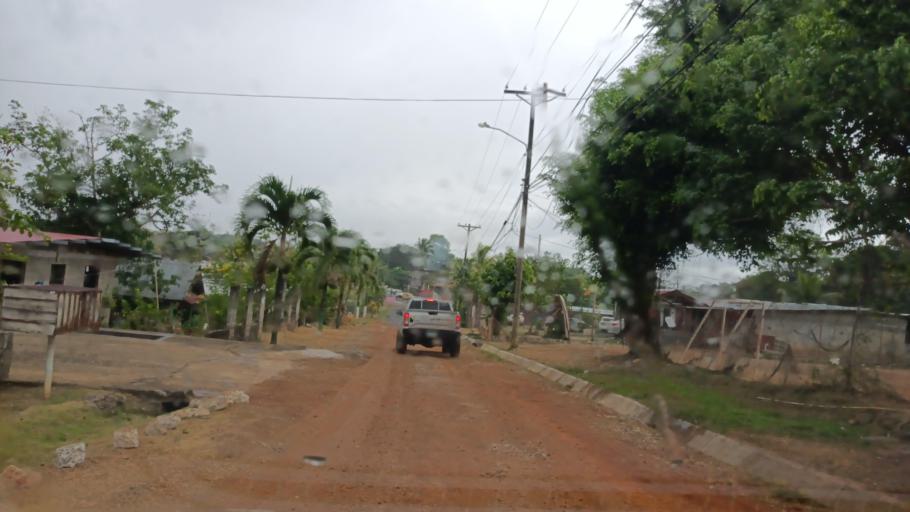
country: PA
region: Panama
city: Caimitillo
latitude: 9.1625
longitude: -79.5493
